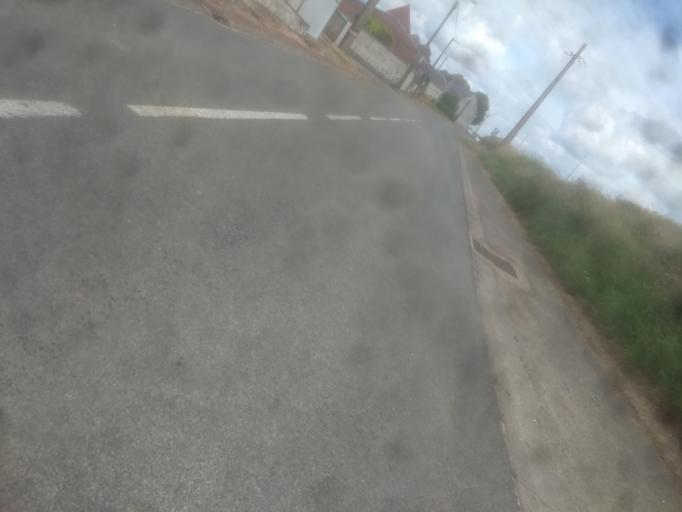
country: FR
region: Nord-Pas-de-Calais
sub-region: Departement du Pas-de-Calais
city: Duisans
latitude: 50.3071
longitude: 2.6613
